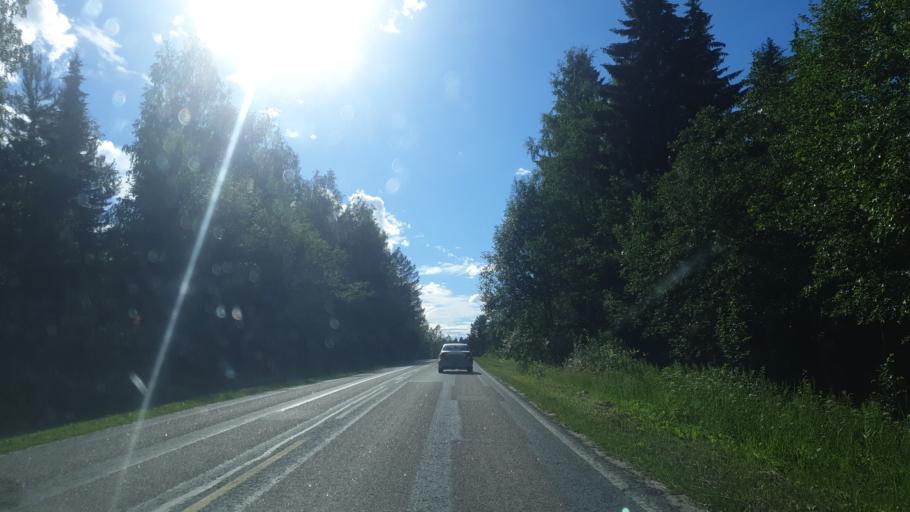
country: FI
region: Southern Savonia
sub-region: Mikkeli
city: Pertunmaa
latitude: 61.5229
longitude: 26.5534
